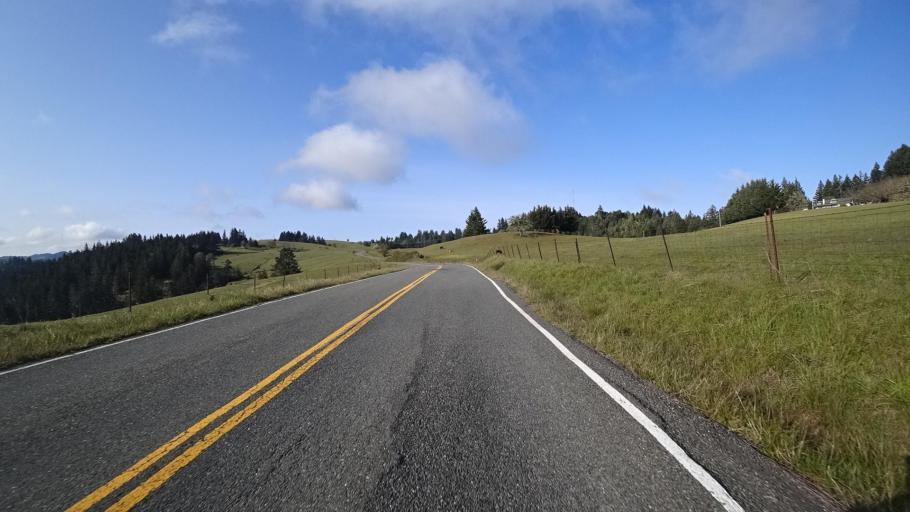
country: US
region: California
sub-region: Humboldt County
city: Blue Lake
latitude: 40.7352
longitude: -123.9463
